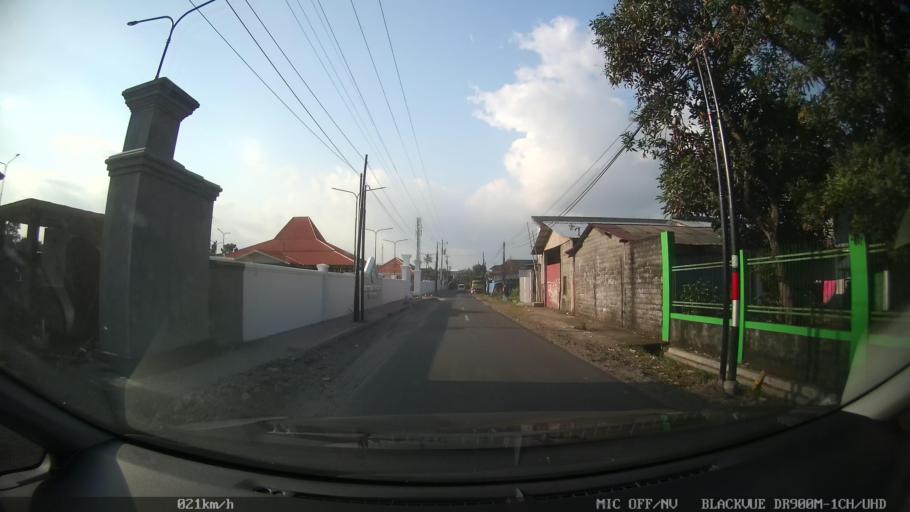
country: ID
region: Daerah Istimewa Yogyakarta
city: Gamping Lor
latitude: -7.7976
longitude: 110.3361
